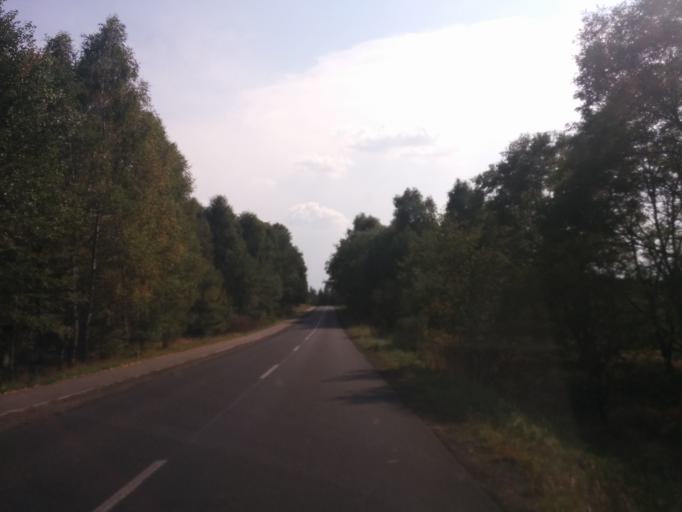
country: PL
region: Silesian Voivodeship
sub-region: Powiat czestochowski
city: Olsztyn
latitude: 50.7378
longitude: 19.2651
